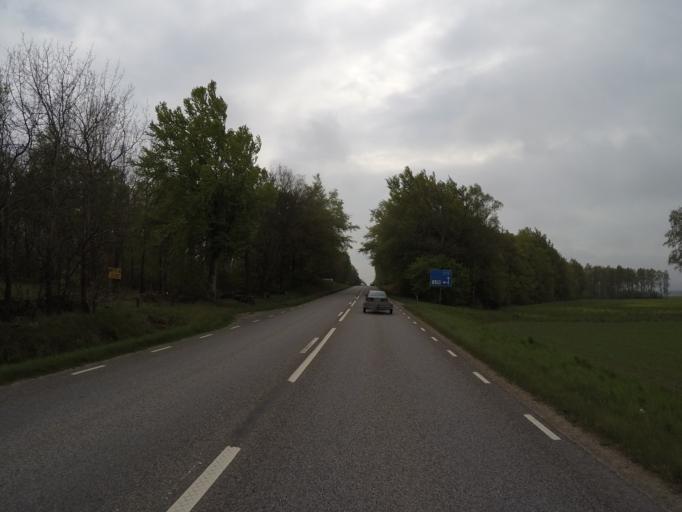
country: SE
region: Halland
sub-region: Laholms Kommun
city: Laholm
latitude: 56.4389
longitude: 13.1165
